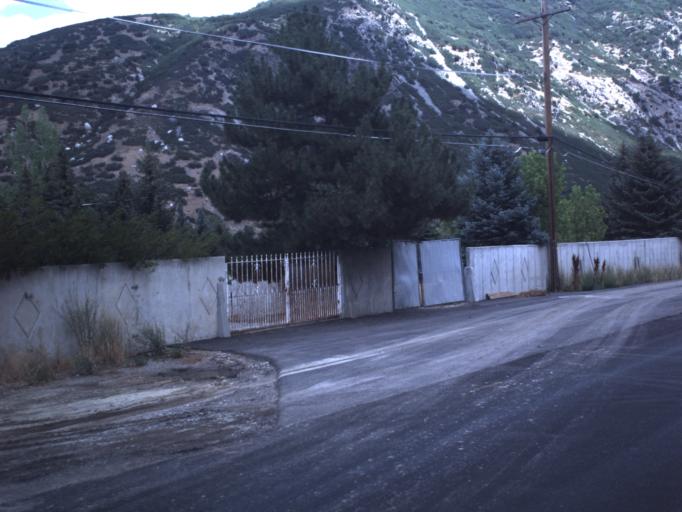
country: US
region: Utah
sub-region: Salt Lake County
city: Granite
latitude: 40.5728
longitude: -111.7917
